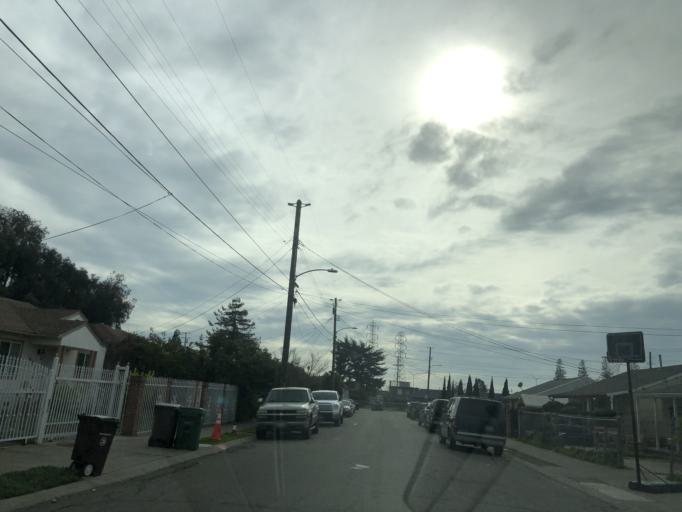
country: US
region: California
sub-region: Alameda County
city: San Leandro
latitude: 37.7380
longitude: -122.1912
